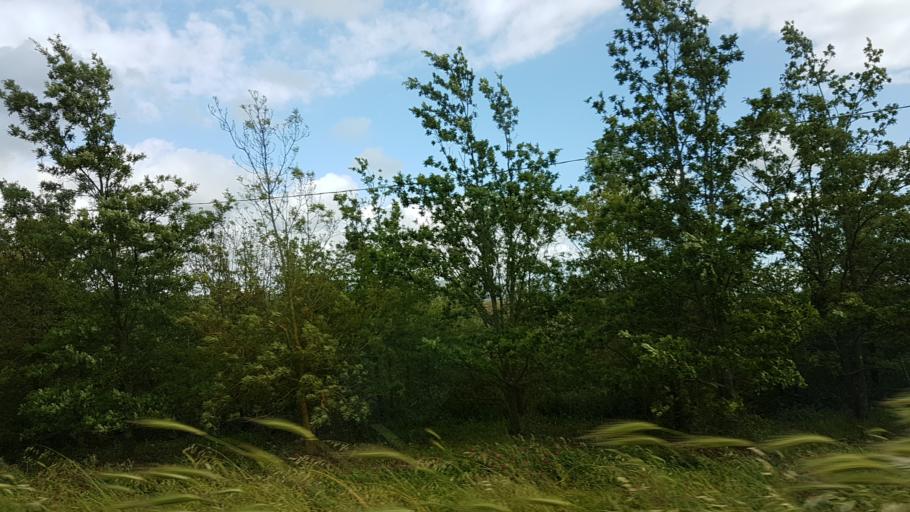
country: IT
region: Tuscany
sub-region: Province of Pisa
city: Santa Luce
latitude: 43.4653
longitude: 10.5425
